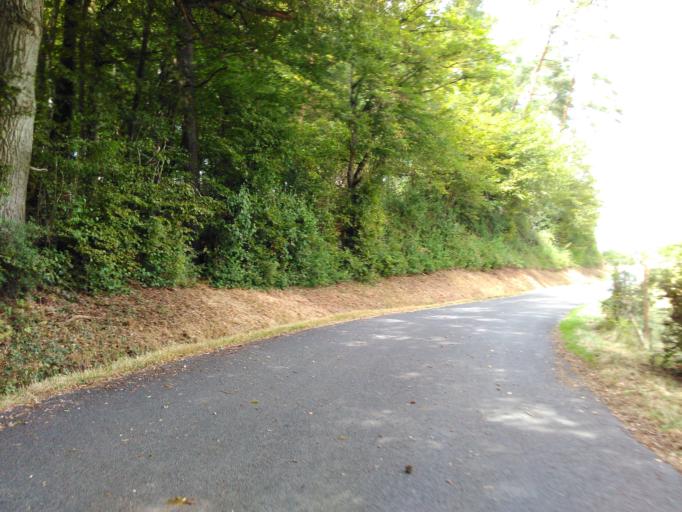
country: LU
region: Grevenmacher
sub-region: Canton de Grevenmacher
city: Junglinster
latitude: 49.7066
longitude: 6.2688
